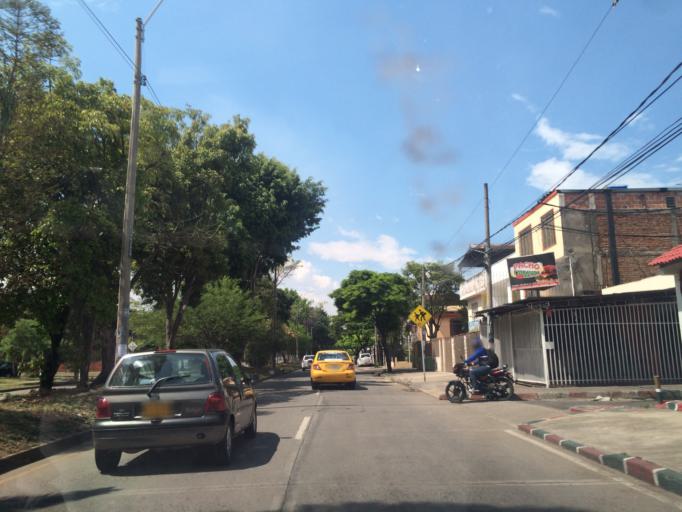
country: CO
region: Valle del Cauca
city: Cali
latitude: 3.4081
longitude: -76.5264
